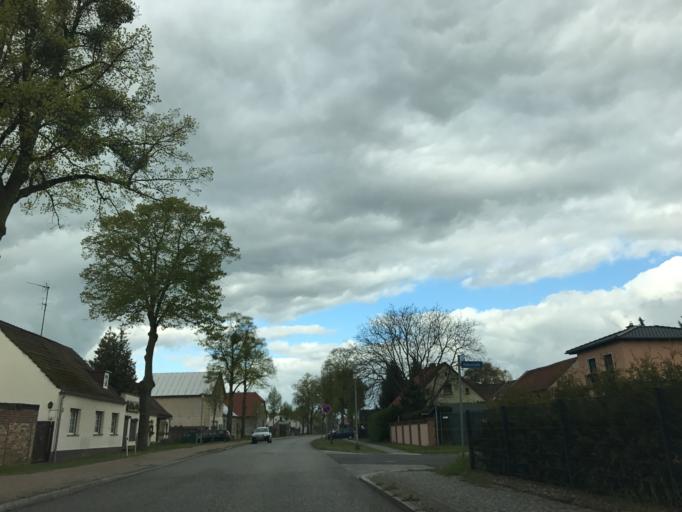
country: DE
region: Brandenburg
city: Wustermark
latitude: 52.5425
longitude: 12.9597
